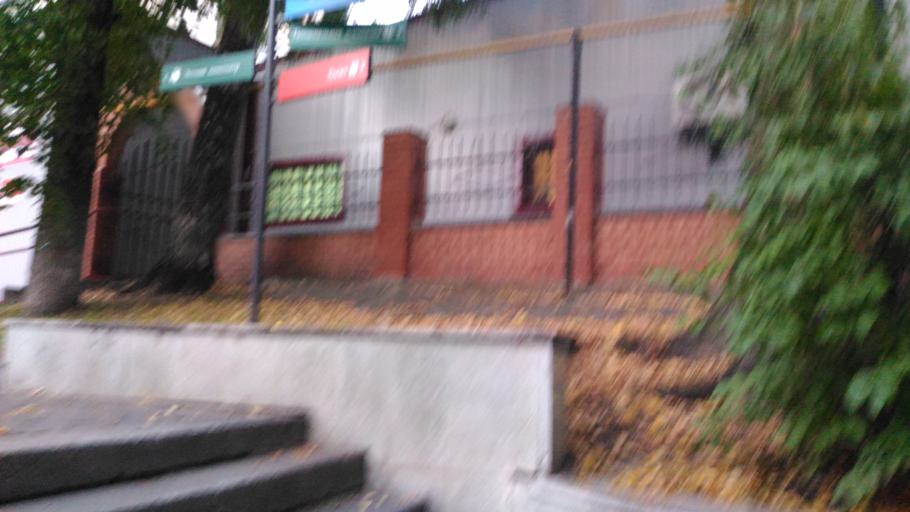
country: RU
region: Ulyanovsk
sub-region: Ulyanovskiy Rayon
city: Ulyanovsk
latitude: 54.3125
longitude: 48.4042
